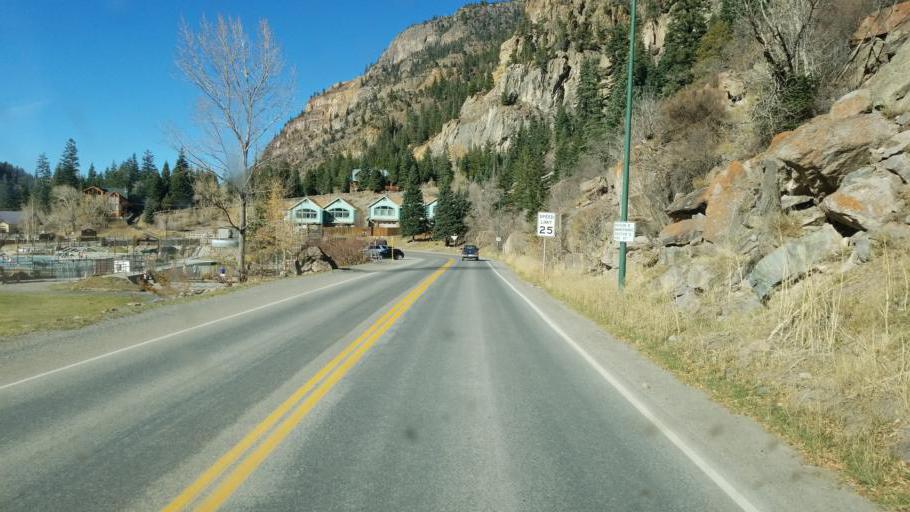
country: US
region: Colorado
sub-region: Ouray County
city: Ouray
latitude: 38.0282
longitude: -107.6715
